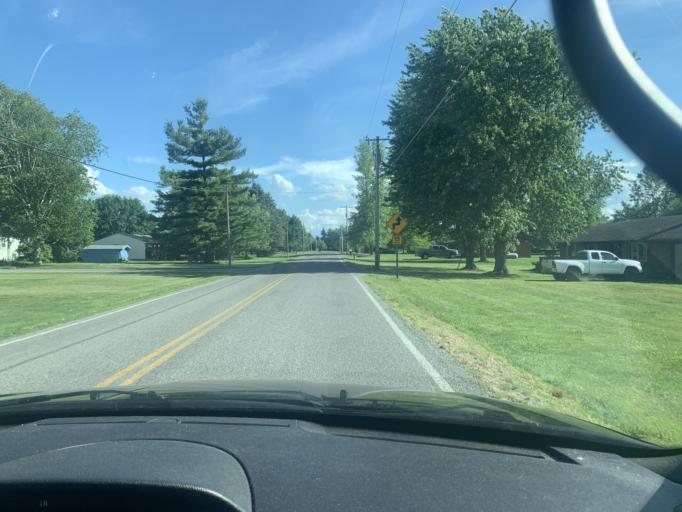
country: US
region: Ohio
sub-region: Logan County
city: Bellefontaine
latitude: 40.3494
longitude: -83.8177
